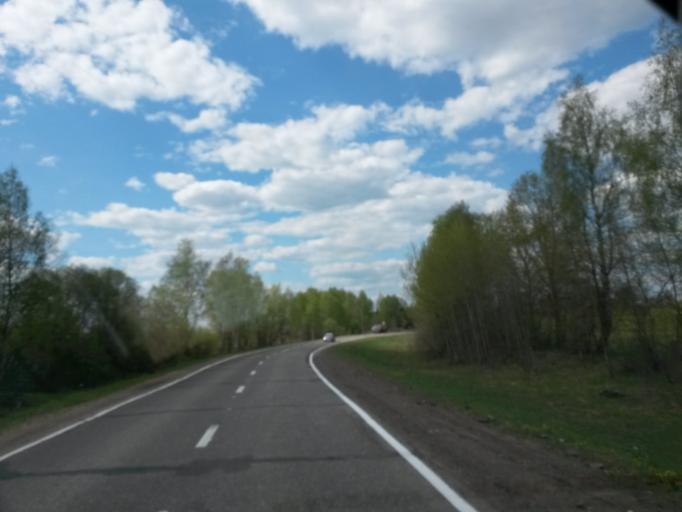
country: RU
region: Jaroslavl
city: Bol'shoye Selo
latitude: 57.6873
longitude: 39.2024
